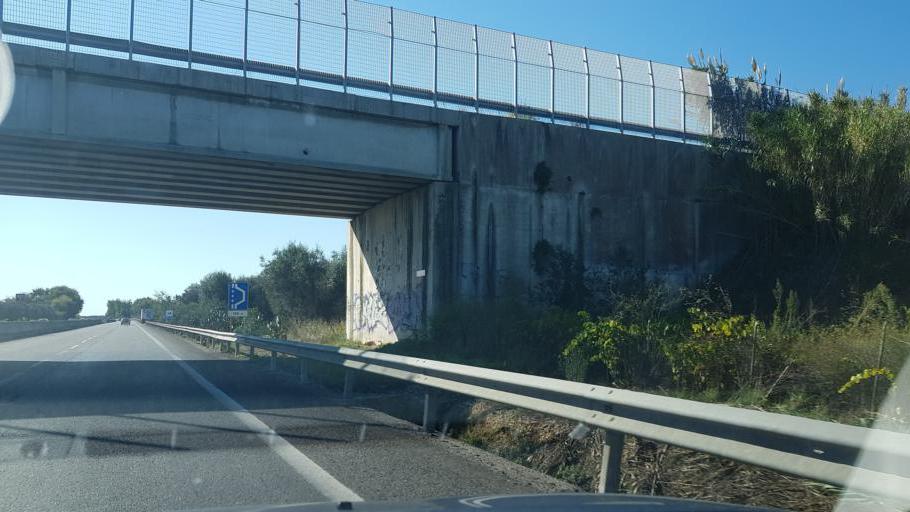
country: IT
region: Apulia
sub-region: Provincia di Brindisi
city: San Pietro Vernotico
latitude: 40.5110
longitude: 18.0237
